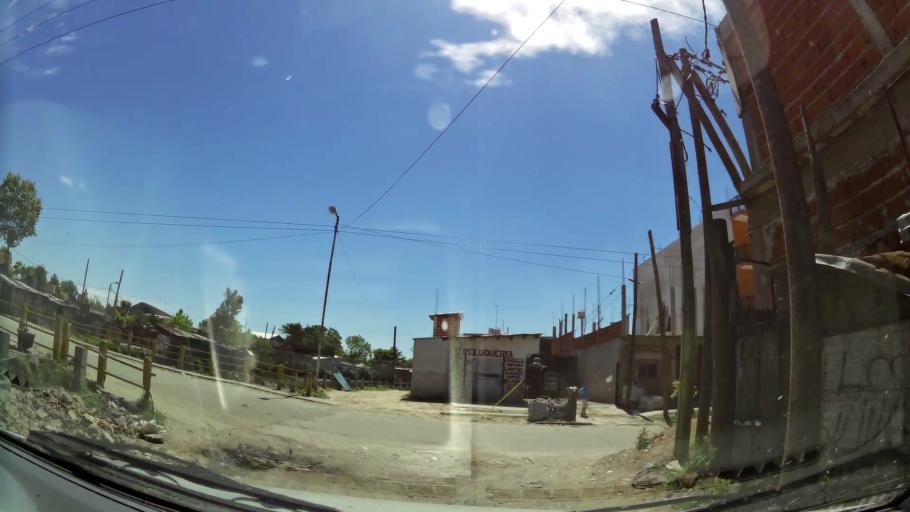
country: AR
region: Buenos Aires
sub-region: Partido de Quilmes
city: Quilmes
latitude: -34.7287
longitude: -58.3192
